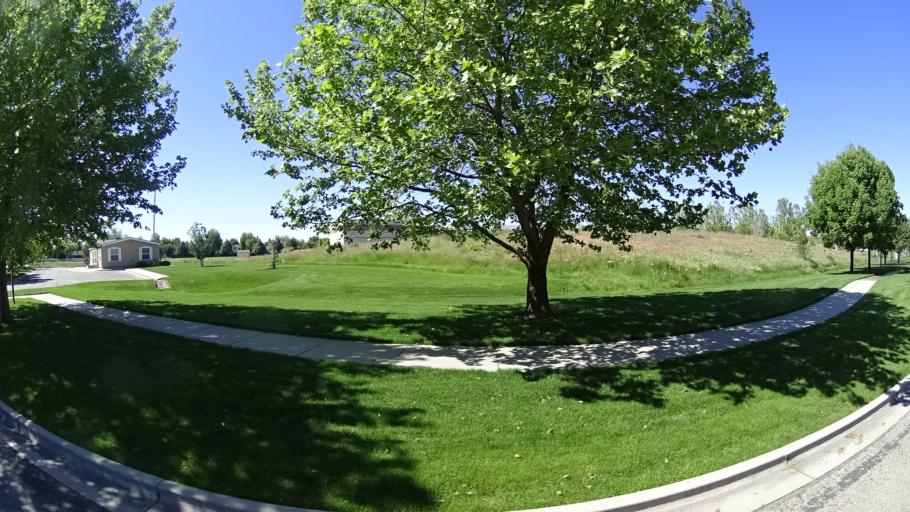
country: US
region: Idaho
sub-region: Ada County
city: Meridian
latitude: 43.6409
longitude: -116.3707
